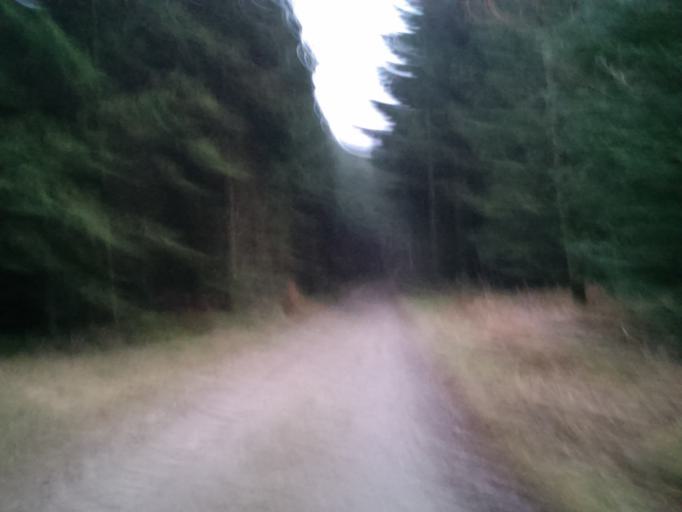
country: DK
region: North Denmark
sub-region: Mariagerfjord Kommune
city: Arden
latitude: 56.7959
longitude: 9.7569
